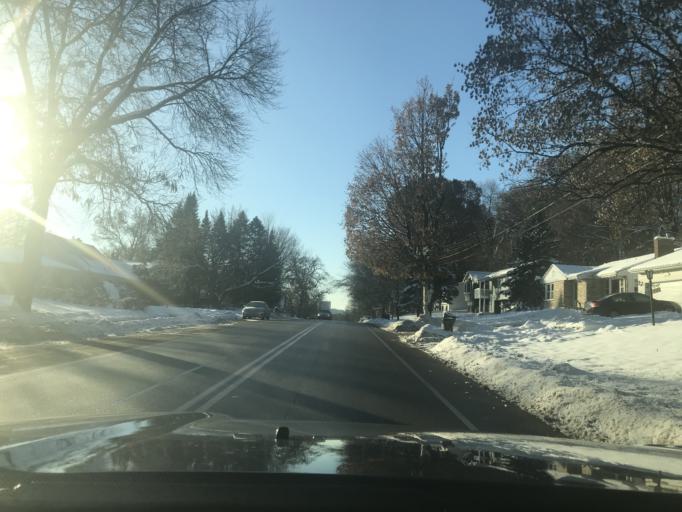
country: US
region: Minnesota
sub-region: Dakota County
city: Mendota Heights
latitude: 44.9234
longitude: -93.1467
